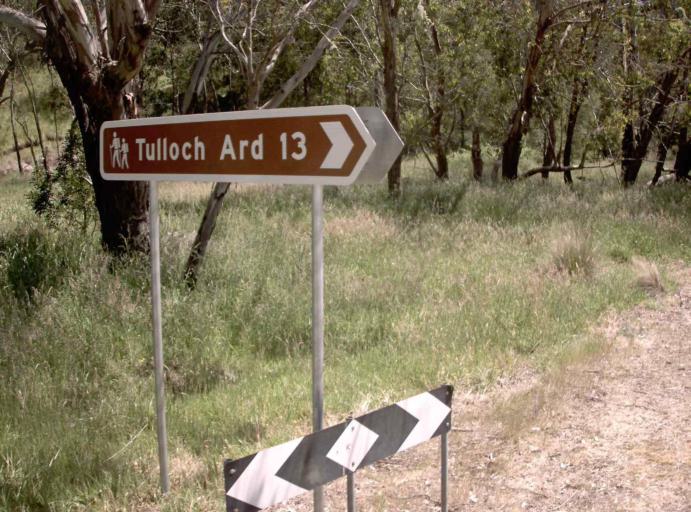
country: AU
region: Victoria
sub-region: East Gippsland
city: Lakes Entrance
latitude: -37.2298
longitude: 148.2629
